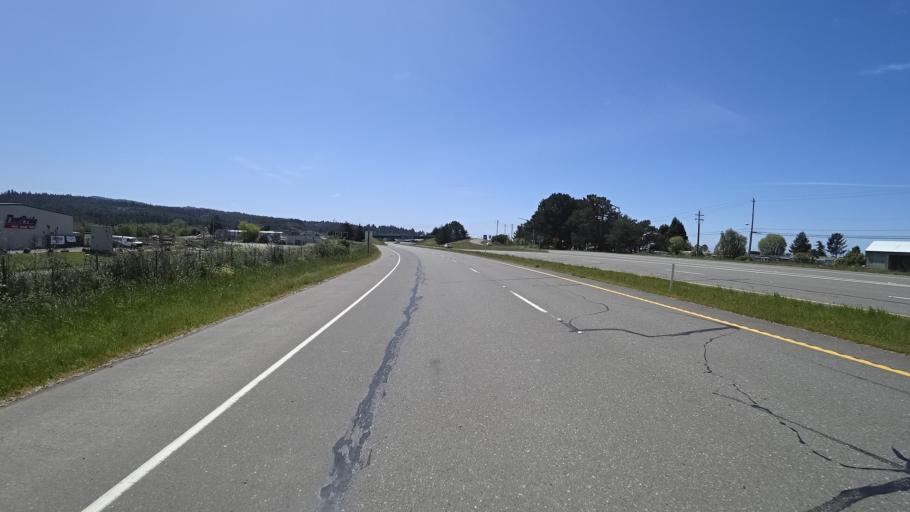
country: US
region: California
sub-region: Humboldt County
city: Arcata
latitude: 40.9069
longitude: -124.0728
